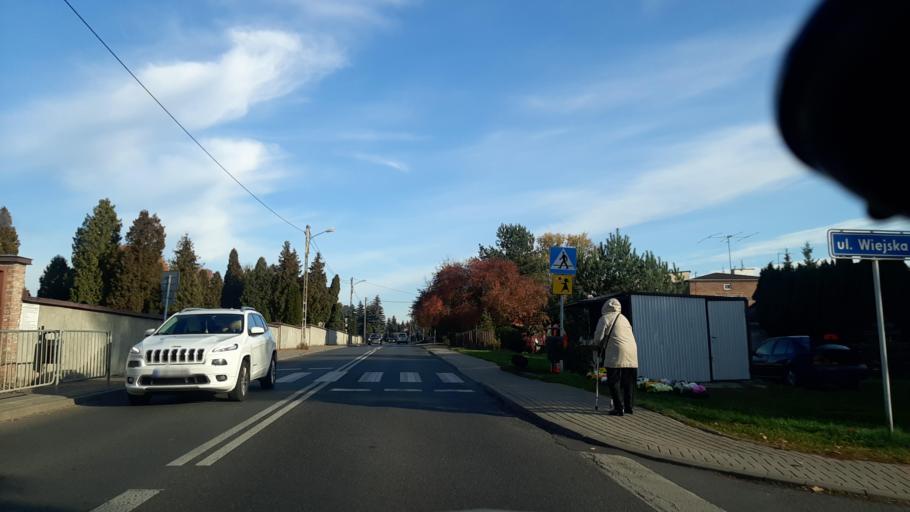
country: PL
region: Lublin Voivodeship
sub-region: Powiat lubelski
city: Lublin
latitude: 51.2635
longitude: 22.5810
